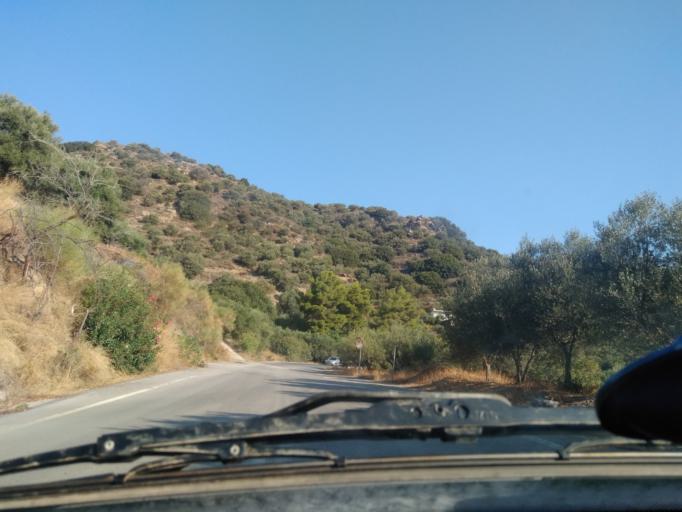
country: GR
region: Crete
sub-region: Nomos Lasithiou
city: Makry-Gialos
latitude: 35.1624
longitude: 25.9690
